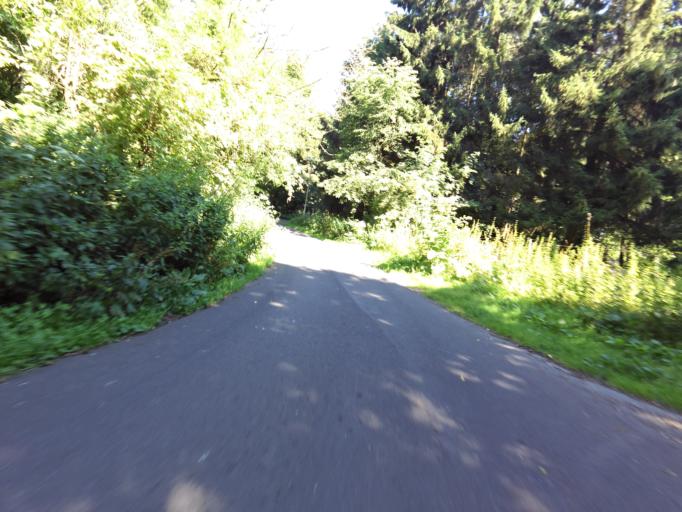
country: NL
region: Limburg
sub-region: Gemeente Kerkrade
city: Kerkrade
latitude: 50.8458
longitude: 6.0831
